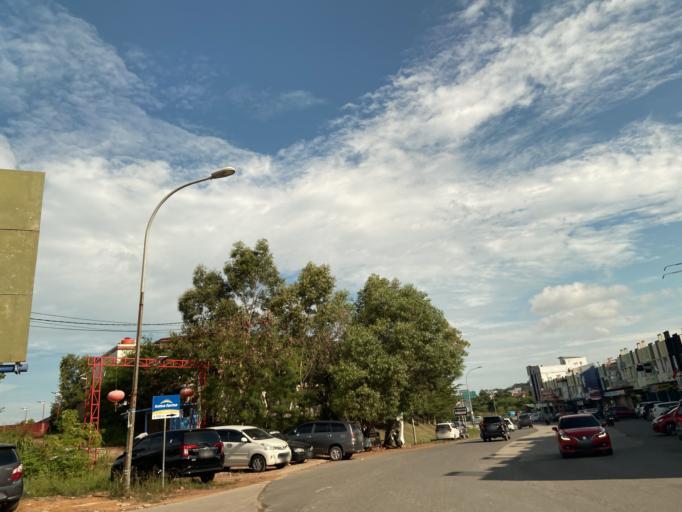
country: SG
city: Singapore
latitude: 1.1087
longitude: 104.0792
